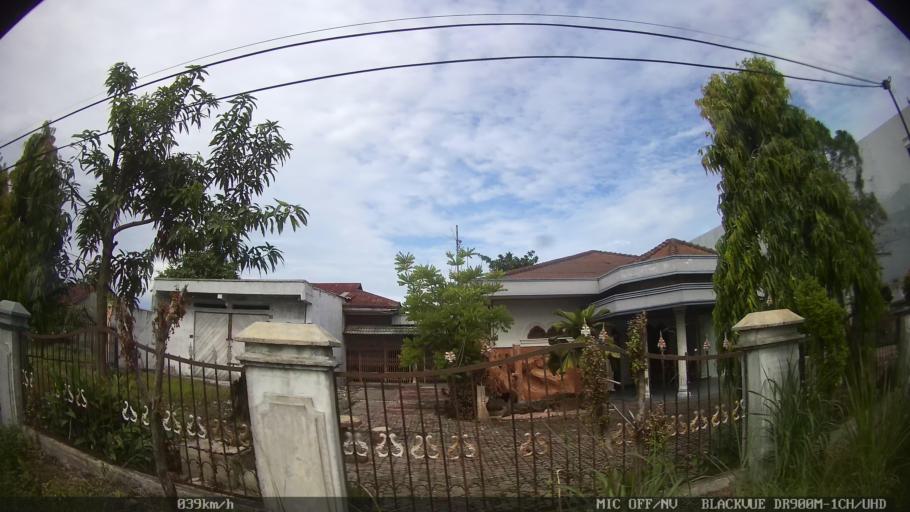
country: ID
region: North Sumatra
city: Sunggal
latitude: 3.5984
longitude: 98.5833
